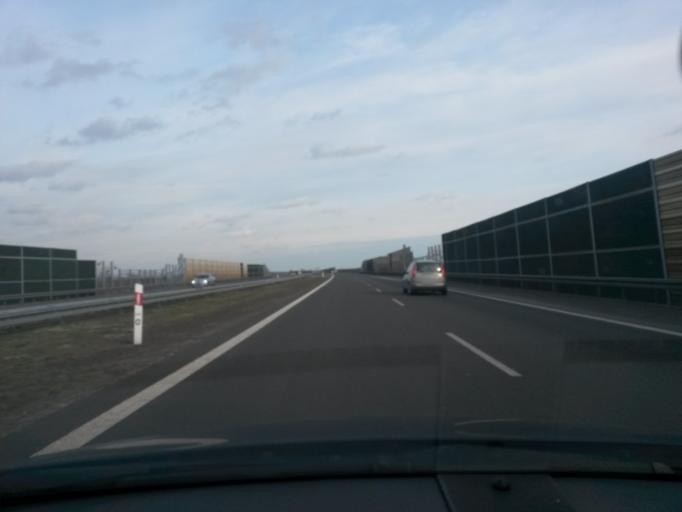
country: PL
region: Greater Poland Voivodeship
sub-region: Powiat turecki
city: Brudzew
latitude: 52.1231
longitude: 18.6836
